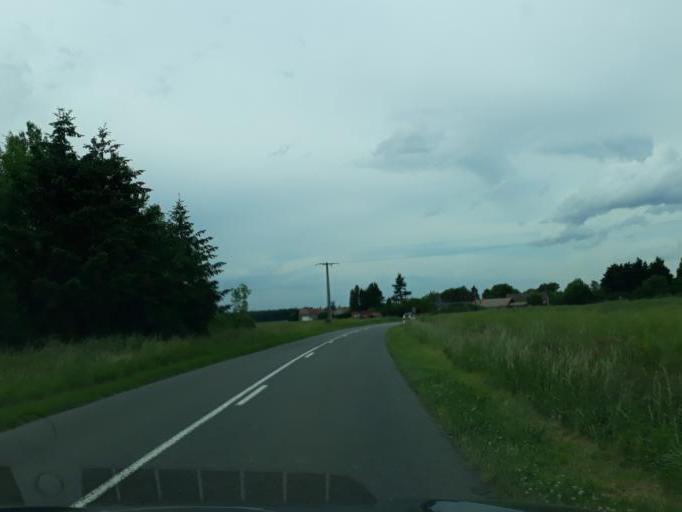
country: FR
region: Centre
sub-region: Departement du Loiret
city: Jargeau
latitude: 47.8410
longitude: 2.1377
